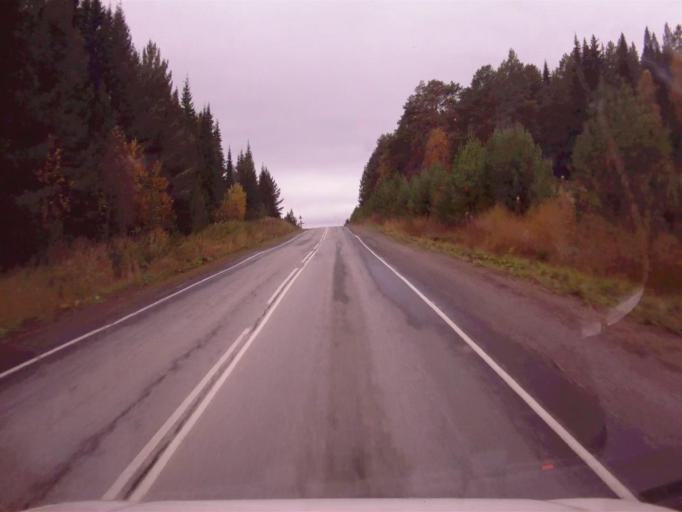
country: RU
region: Chelyabinsk
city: Nyazepetrovsk
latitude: 56.0664
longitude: 59.6727
